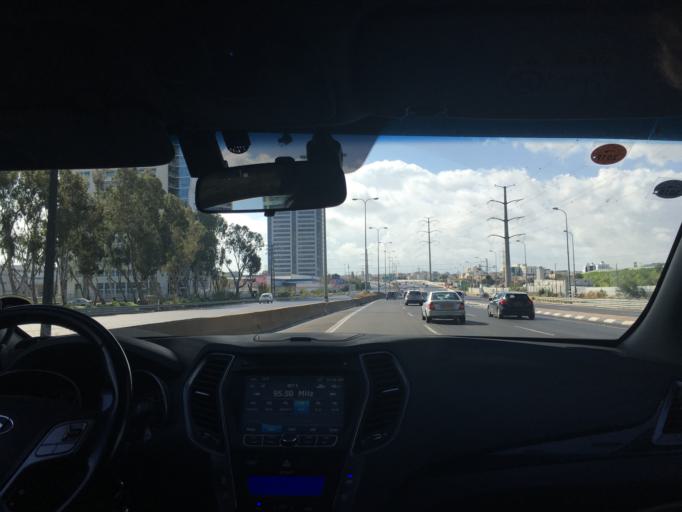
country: IL
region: Tel Aviv
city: Giv`at Shemu'el
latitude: 32.1006
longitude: 34.8477
